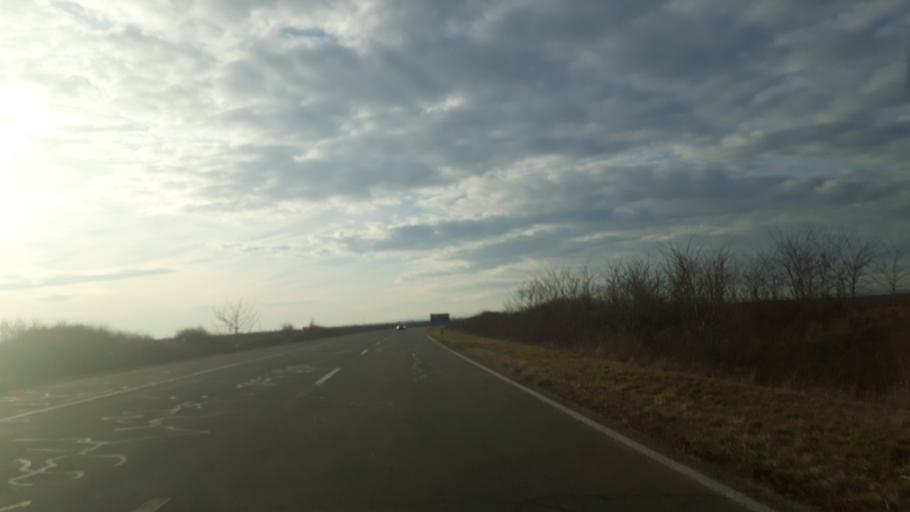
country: RS
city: Beska
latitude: 45.0909
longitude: 20.0447
